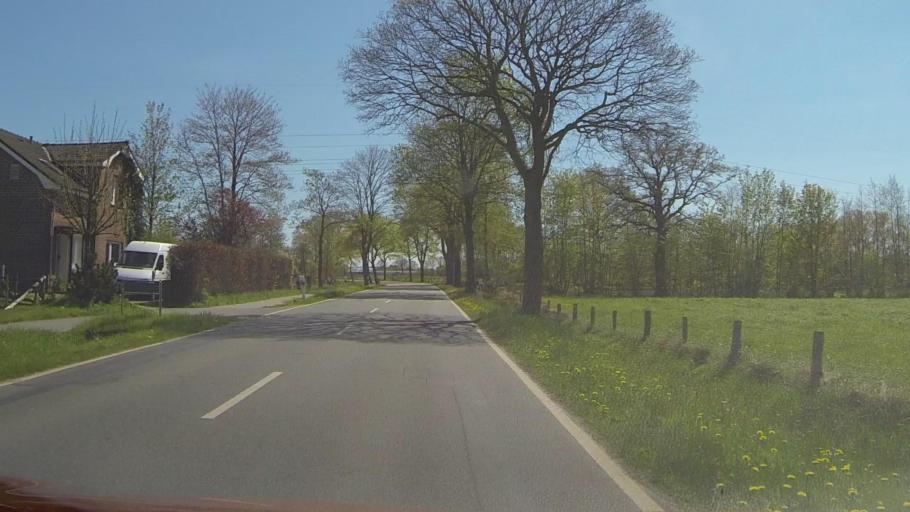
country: DE
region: Schleswig-Holstein
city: Ellerbek
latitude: 53.6526
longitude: 9.8700
